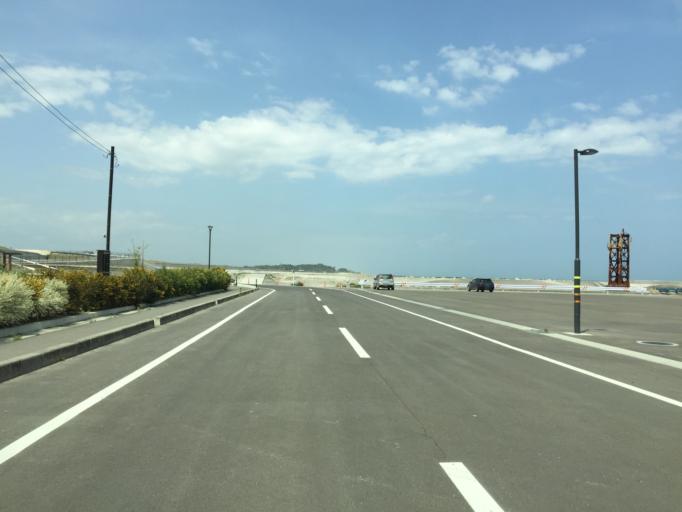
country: JP
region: Miyagi
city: Marumori
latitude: 37.8747
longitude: 140.9355
